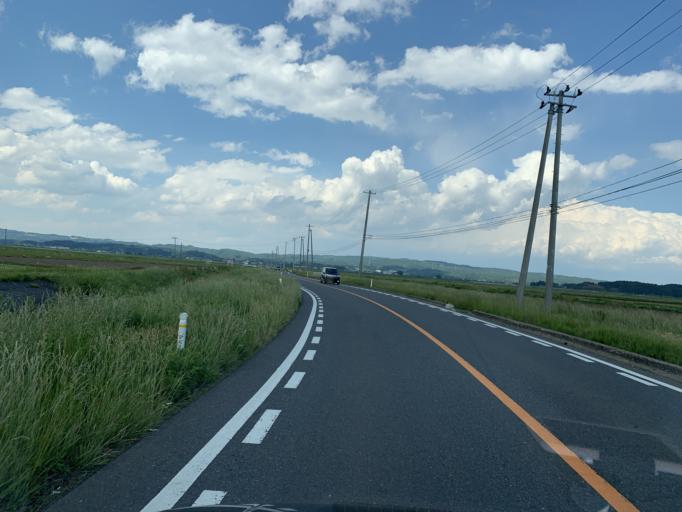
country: JP
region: Miyagi
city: Wakuya
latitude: 38.5141
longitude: 141.1257
